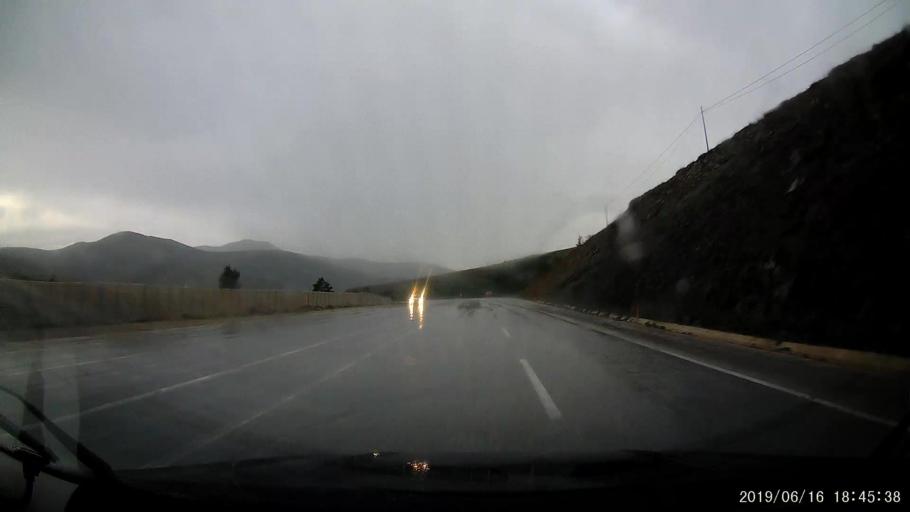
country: TR
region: Erzincan
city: Doganbeyli
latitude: 39.8711
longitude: 39.0529
